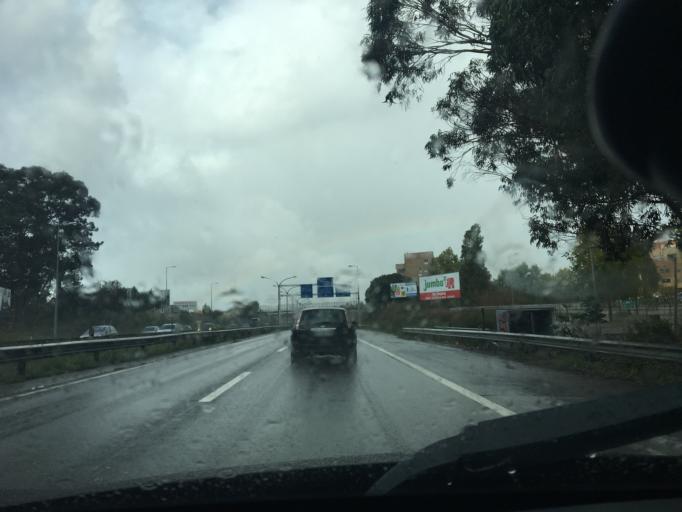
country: PT
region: Porto
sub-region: Matosinhos
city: Senhora da Hora
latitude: 41.1849
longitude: -8.6638
